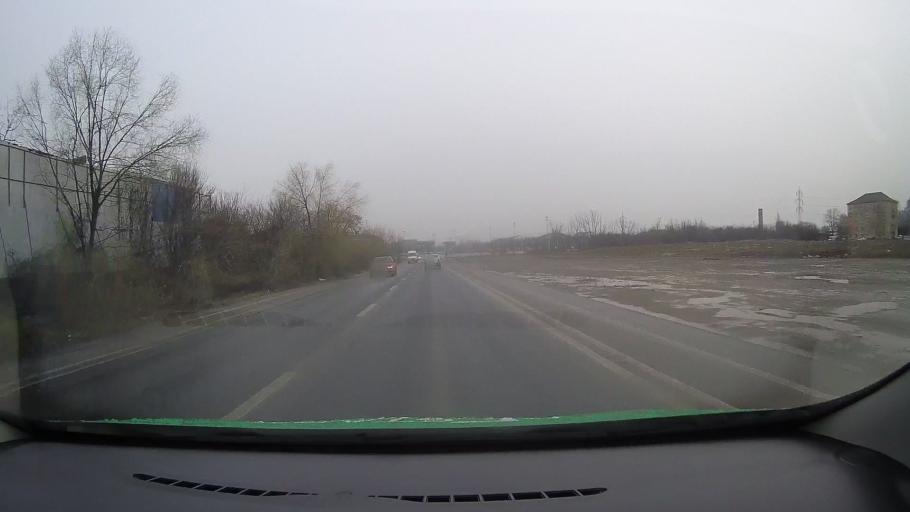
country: RO
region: Timis
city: Timisoara
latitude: 45.7395
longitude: 21.2500
